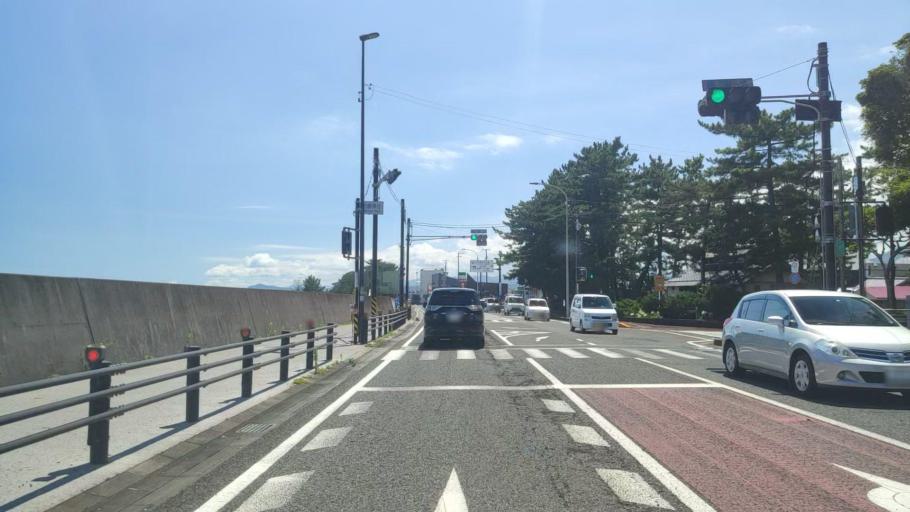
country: JP
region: Wakayama
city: Shingu
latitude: 33.8789
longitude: 136.0929
